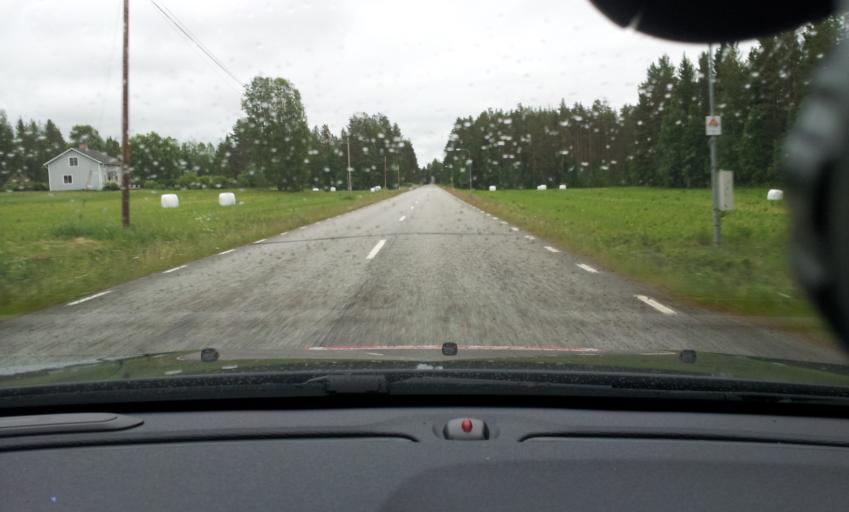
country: SE
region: Jaemtland
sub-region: Ragunda Kommun
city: Hammarstrand
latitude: 63.2248
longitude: 15.9313
